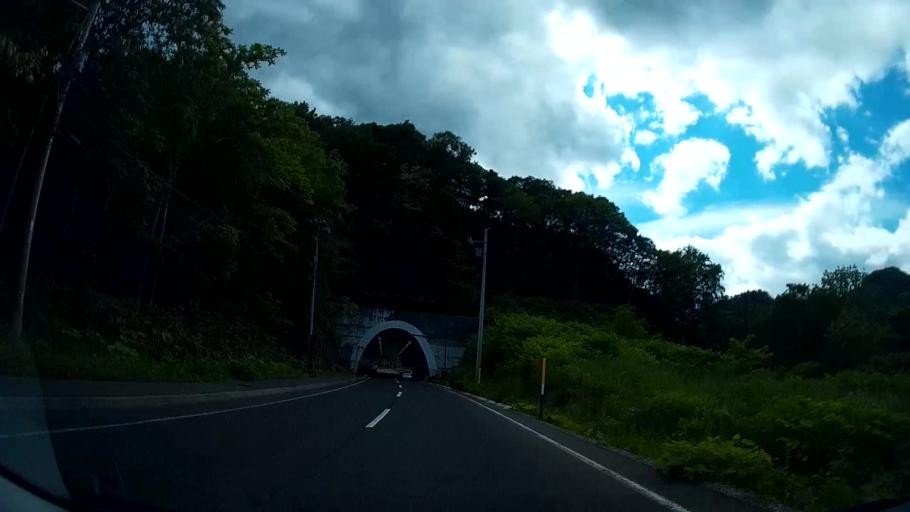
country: JP
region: Hokkaido
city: Sapporo
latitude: 42.9698
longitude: 141.1886
